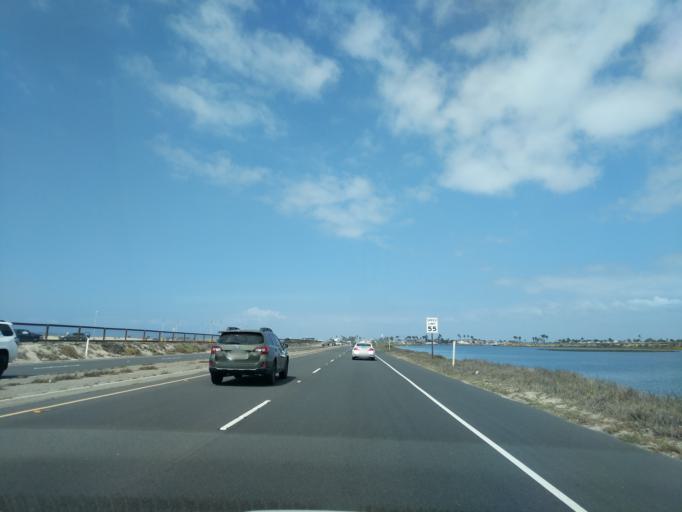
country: US
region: California
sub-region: Orange County
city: Seal Beach
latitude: 33.7044
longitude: -118.0556
